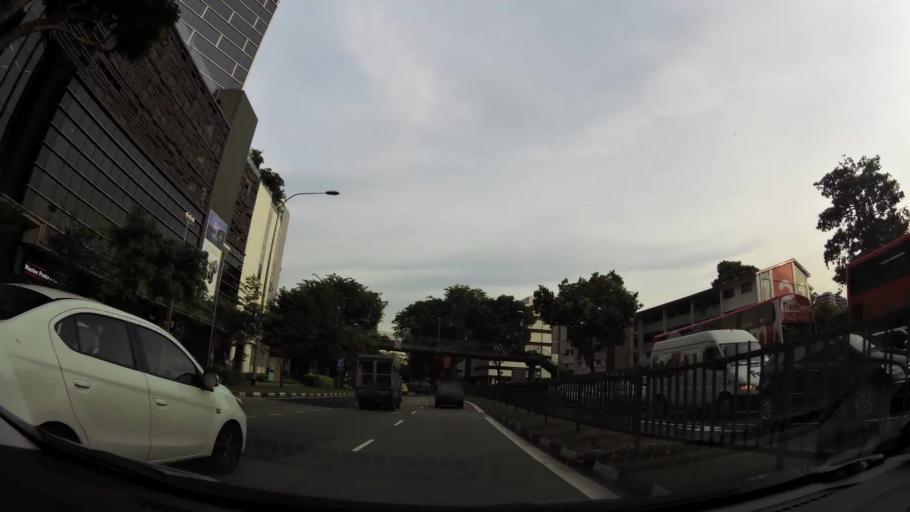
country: SG
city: Singapore
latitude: 1.2872
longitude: 103.8048
